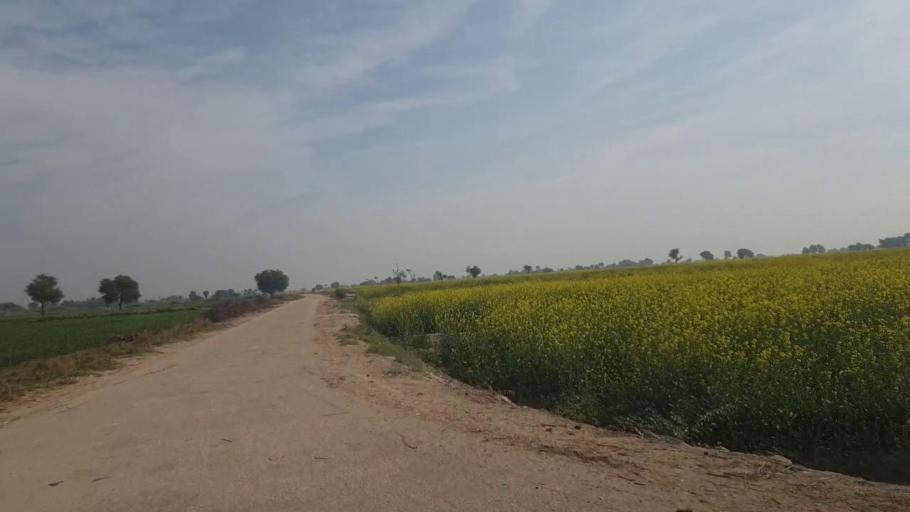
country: PK
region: Sindh
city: Nawabshah
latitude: 26.1240
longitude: 68.4915
